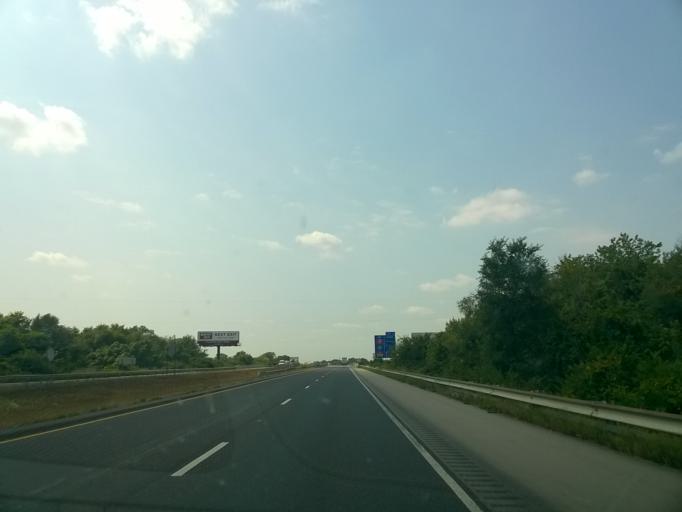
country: US
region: Indiana
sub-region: Vigo County
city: Terre Haute
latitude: 39.4314
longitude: -87.3870
